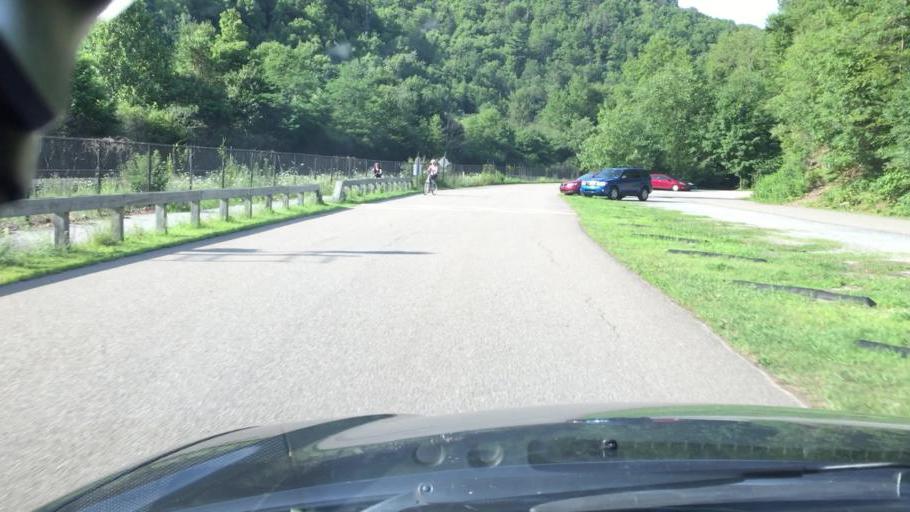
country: US
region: Pennsylvania
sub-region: Carbon County
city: Jim Thorpe
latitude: 40.8815
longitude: -75.7629
